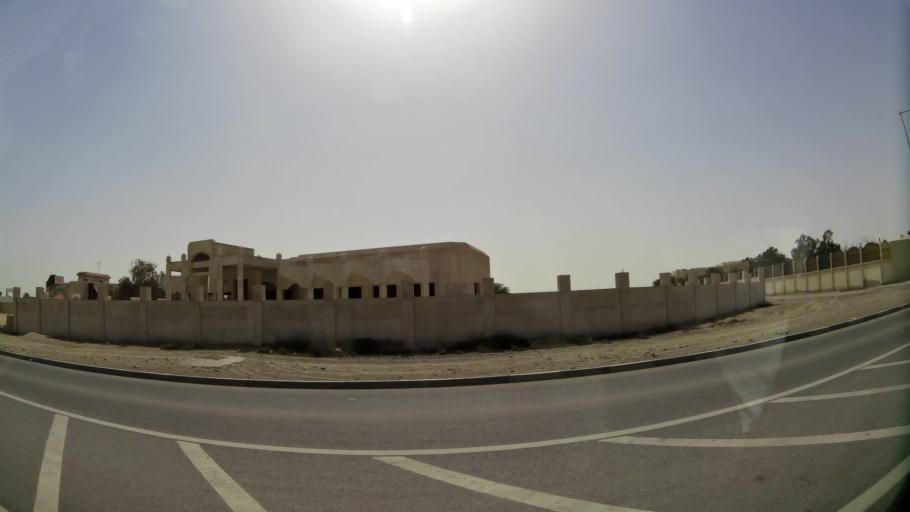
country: QA
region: Baladiyat Umm Salal
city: Umm Salal Muhammad
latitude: 25.4065
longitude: 51.4169
